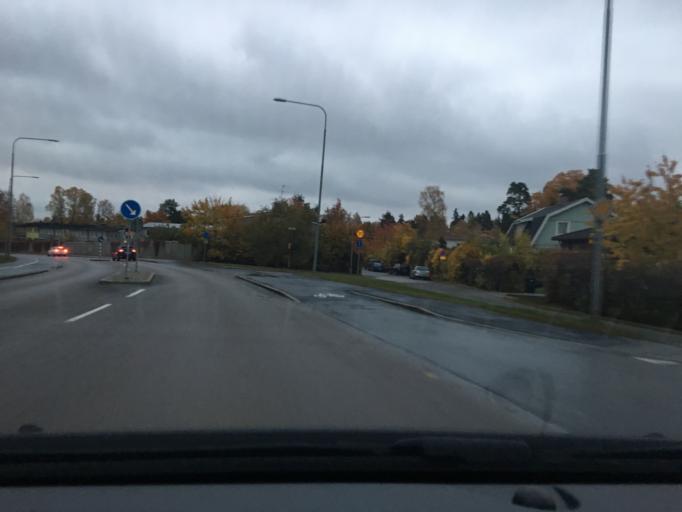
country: SE
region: Stockholm
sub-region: Stockholms Kommun
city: Bromma
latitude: 59.3739
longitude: 17.9028
